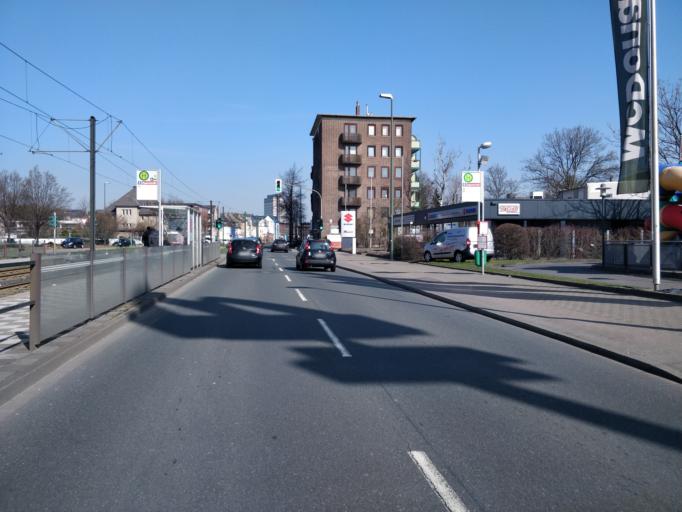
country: DE
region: North Rhine-Westphalia
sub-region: Regierungsbezirk Dusseldorf
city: Neuss
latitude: 51.2253
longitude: 6.6986
